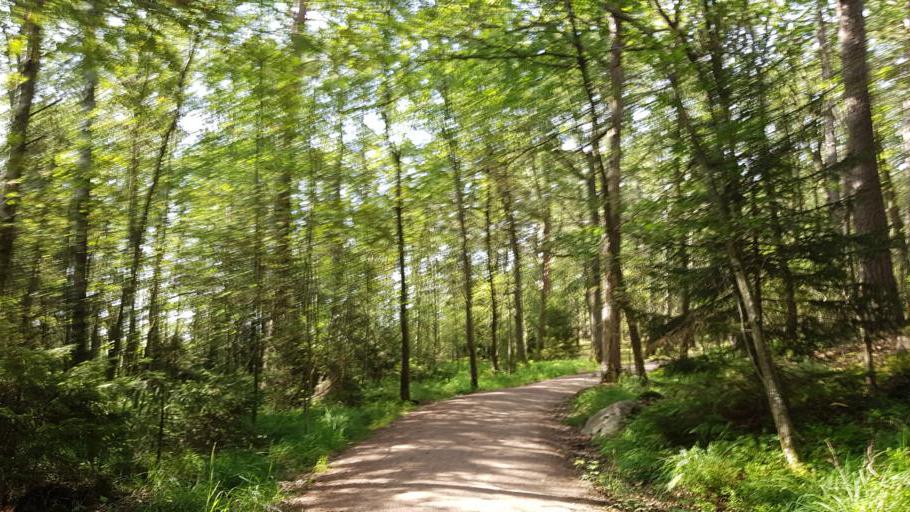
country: SE
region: Vaestra Goetaland
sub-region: Molndal
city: Moelndal
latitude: 57.6900
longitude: 12.0442
